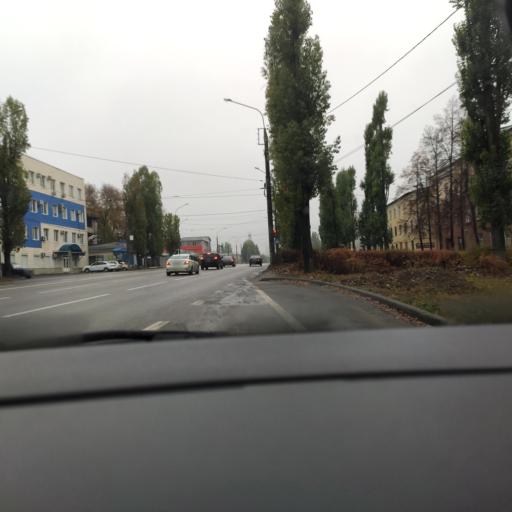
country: RU
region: Voronezj
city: Voronezh
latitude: 51.6888
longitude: 39.1650
